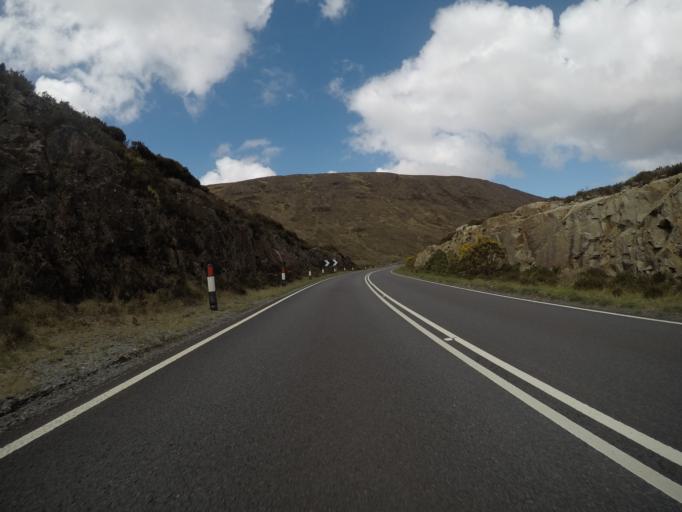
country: GB
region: Scotland
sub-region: Highland
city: Portree
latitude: 57.2625
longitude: -6.0895
